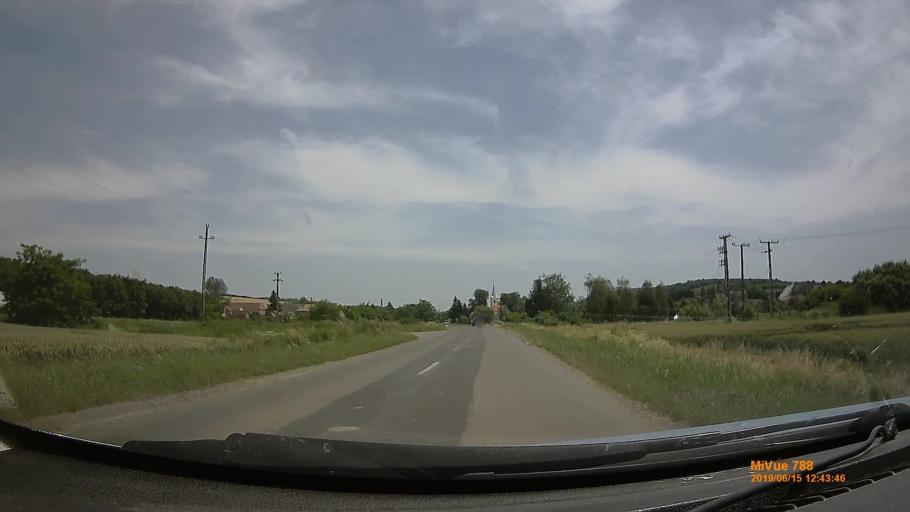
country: HU
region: Baranya
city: Sasd
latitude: 46.2222
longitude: 18.1166
